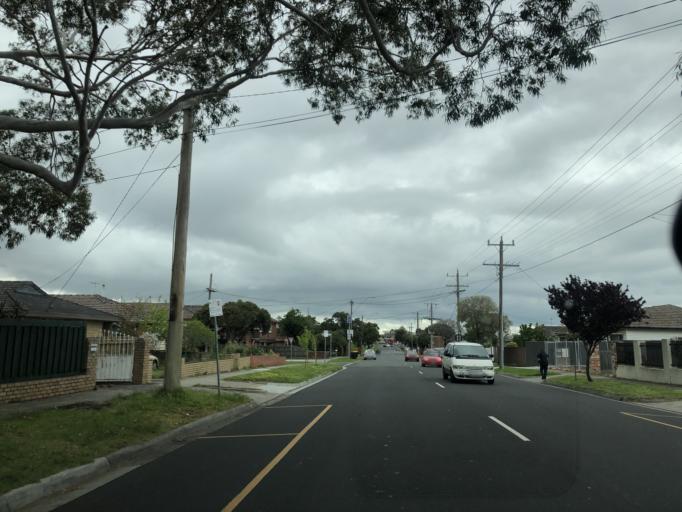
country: AU
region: Victoria
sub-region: Greater Dandenong
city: Dandenong North
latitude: -37.9715
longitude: 145.2046
